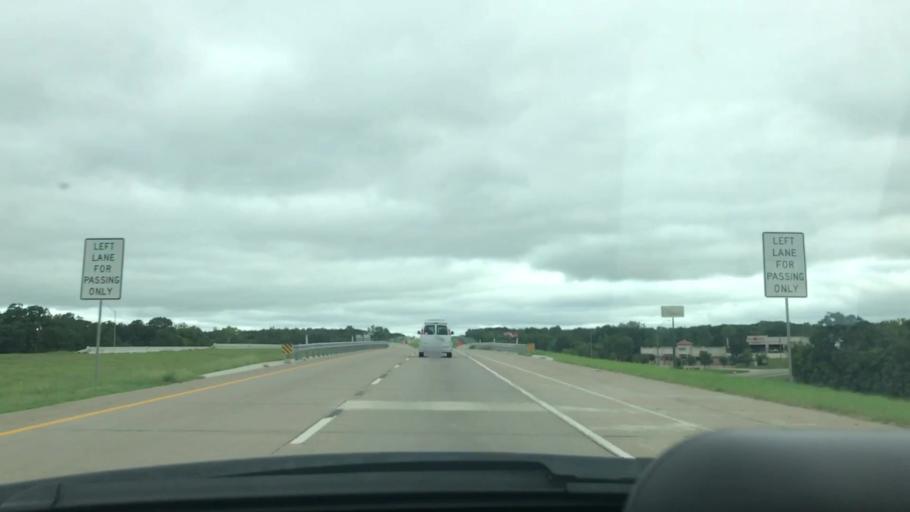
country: US
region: Texas
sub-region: Grayson County
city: Denison
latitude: 33.7275
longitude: -96.5852
